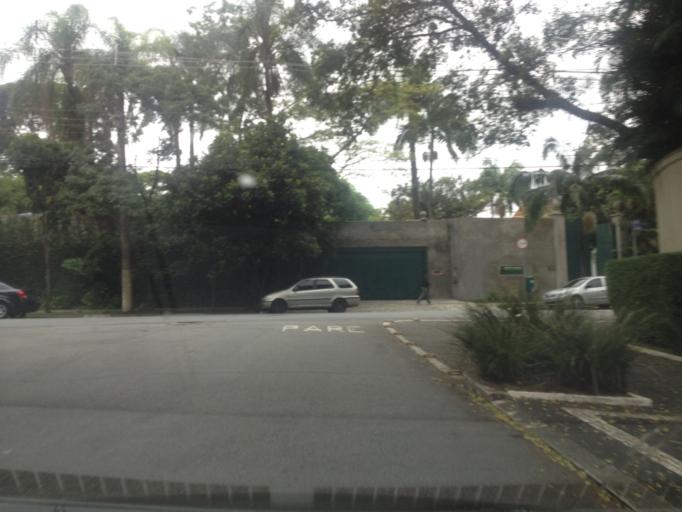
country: BR
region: Sao Paulo
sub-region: Sao Paulo
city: Sao Paulo
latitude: -23.5731
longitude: -46.6720
